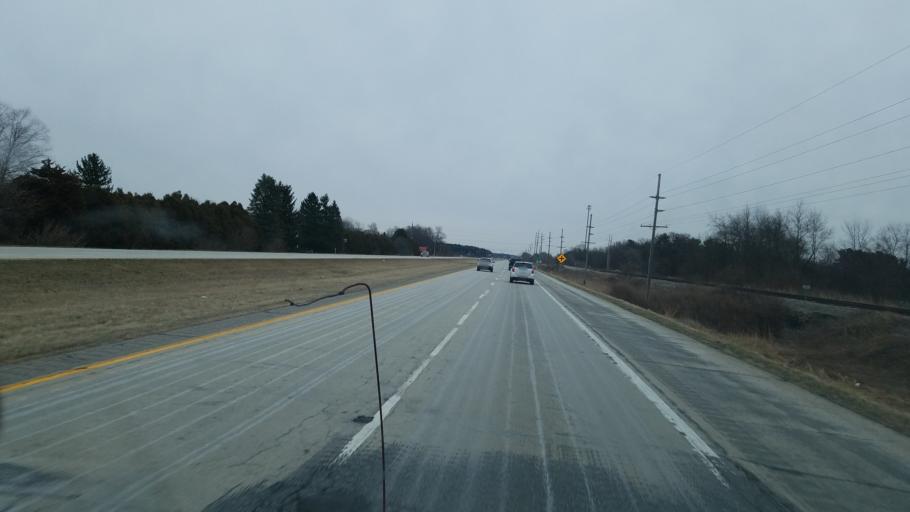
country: US
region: Indiana
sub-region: Starke County
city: Koontz Lake
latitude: 41.3789
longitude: -86.5580
